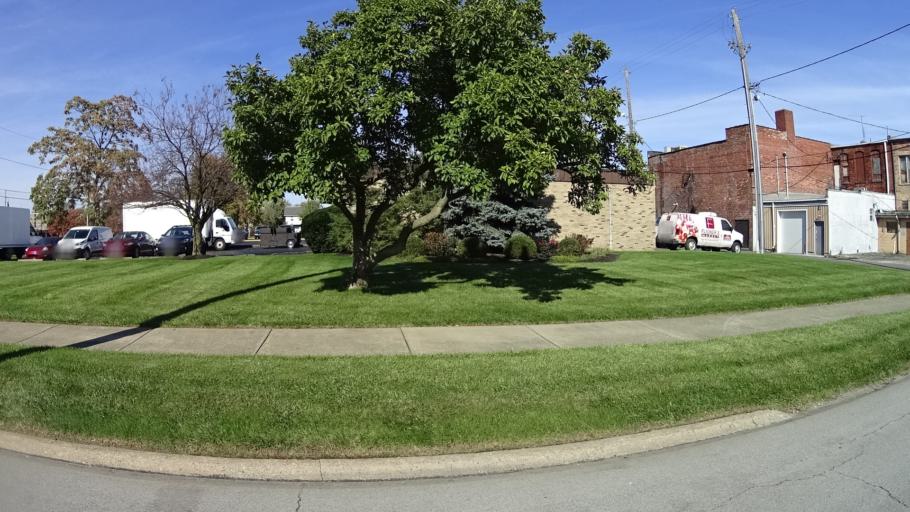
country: US
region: Ohio
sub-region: Lorain County
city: Lorain
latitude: 41.4524
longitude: -82.1671
